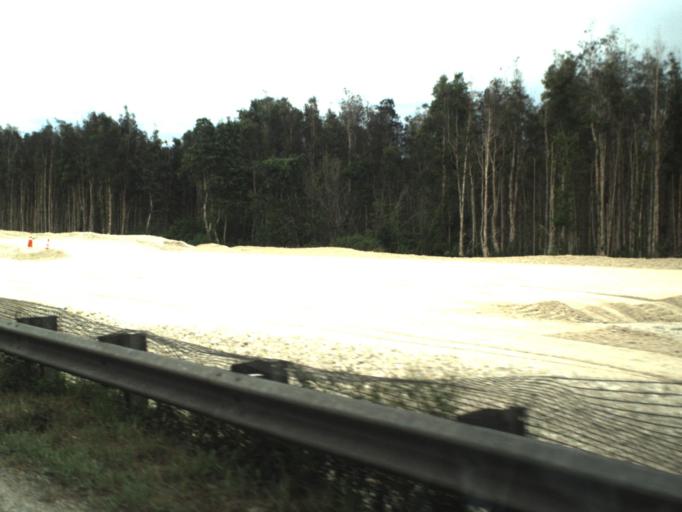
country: US
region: Florida
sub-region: Miami-Dade County
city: Kendall West
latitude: 25.7400
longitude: -80.4806
